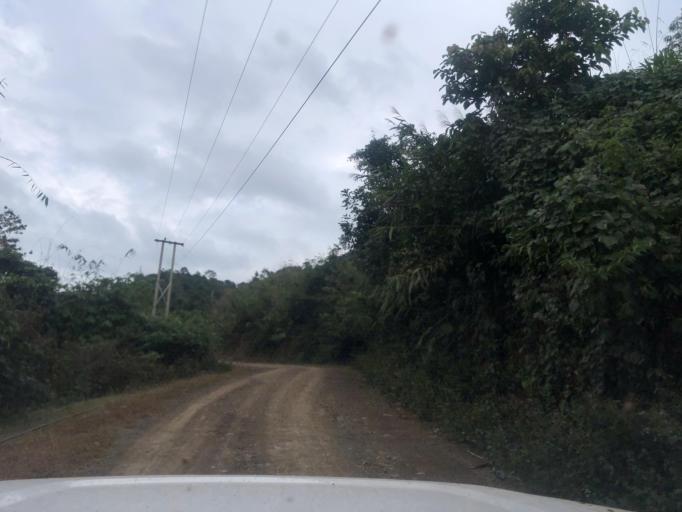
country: LA
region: Phongsali
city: Khoa
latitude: 21.3062
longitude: 102.5823
